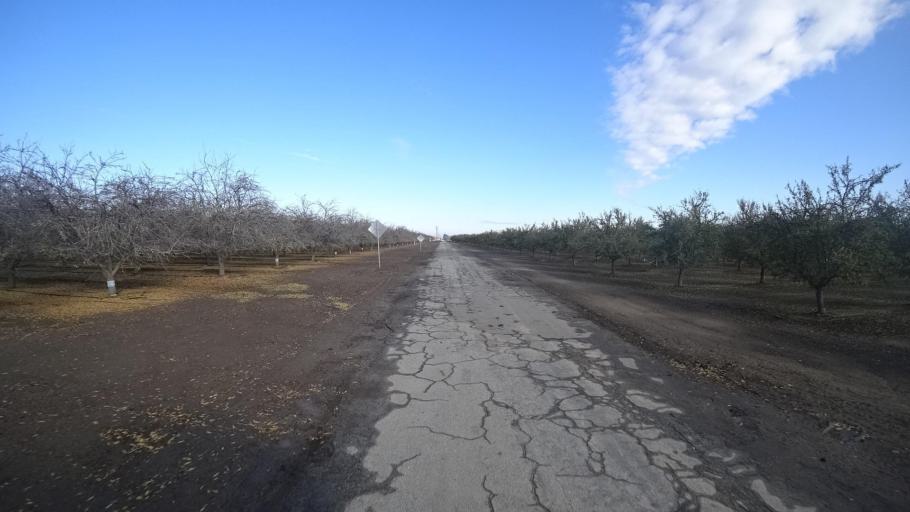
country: US
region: California
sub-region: Kern County
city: McFarland
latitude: 35.7043
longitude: -119.3208
